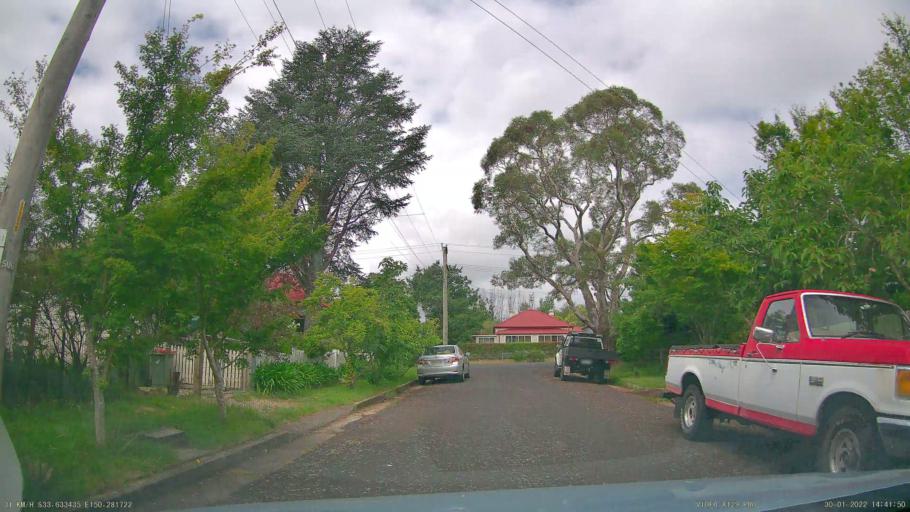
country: AU
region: New South Wales
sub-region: Blue Mountains Municipality
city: Blackheath
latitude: -33.6335
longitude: 150.2819
